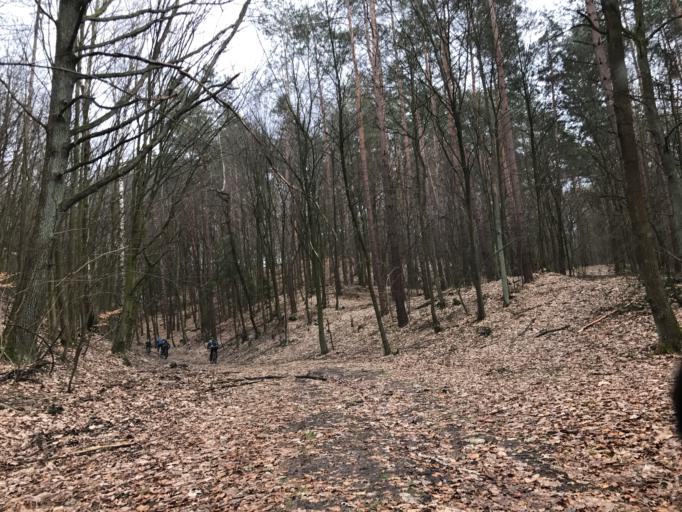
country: PL
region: Kujawsko-Pomorskie
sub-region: Powiat brodnicki
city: Gorzno
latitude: 53.2009
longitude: 19.6696
